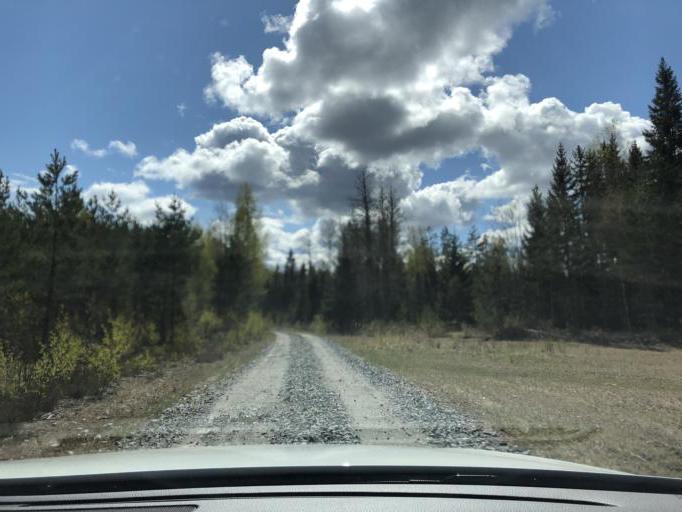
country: SE
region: Uppsala
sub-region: Heby Kommun
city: Tarnsjo
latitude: 60.2394
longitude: 16.7052
